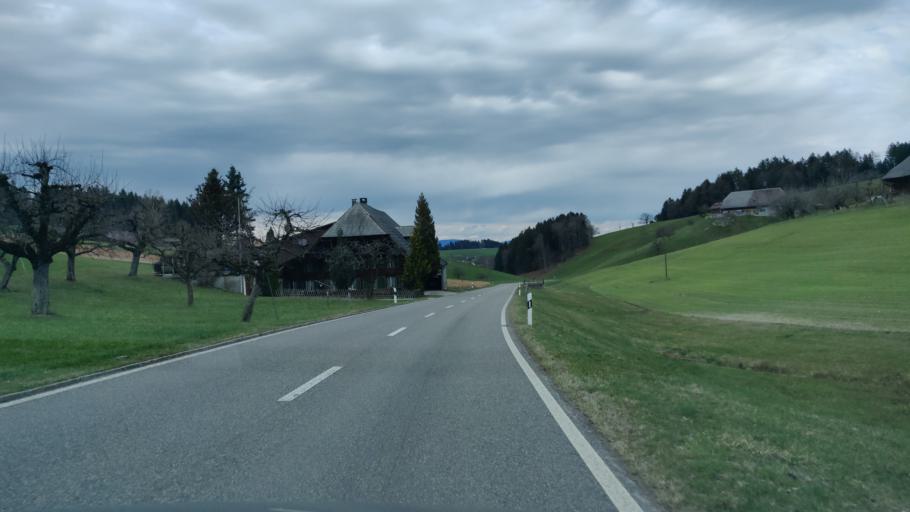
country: CH
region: Bern
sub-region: Emmental District
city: Durrenroth
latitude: 47.0978
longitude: 7.7765
